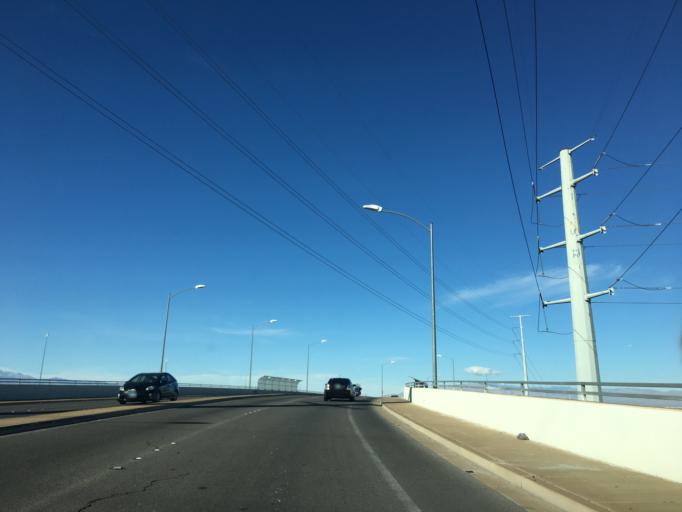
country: US
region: Nevada
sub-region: Clark County
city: Henderson
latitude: 36.0382
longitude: -115.0174
